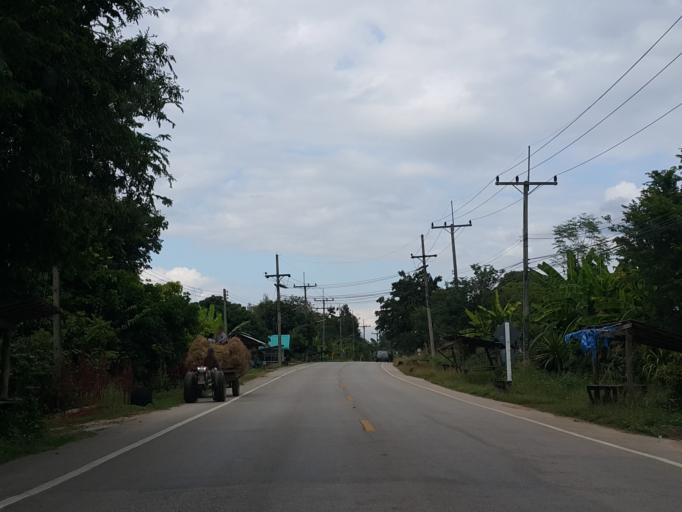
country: TH
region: Lampang
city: Chae Hom
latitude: 18.5956
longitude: 99.4779
